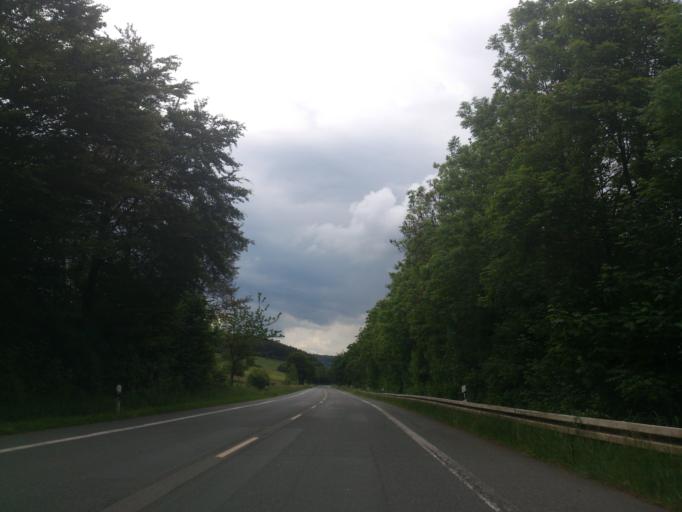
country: DE
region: North Rhine-Westphalia
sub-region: Regierungsbezirk Detmold
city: Willebadessen
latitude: 51.6470
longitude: 9.0127
